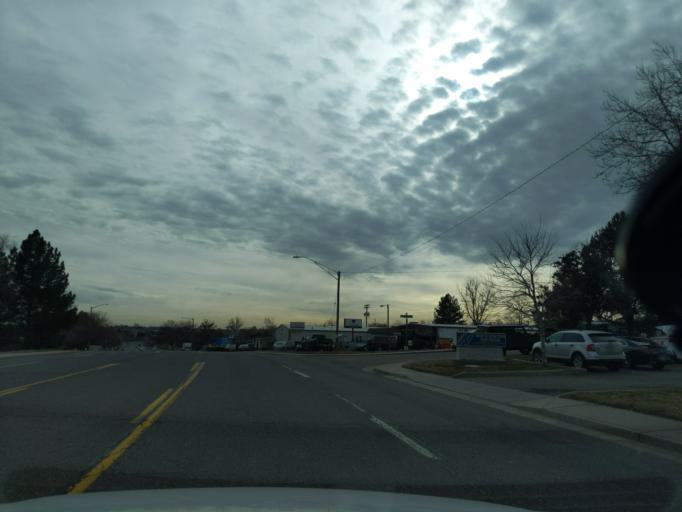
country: US
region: Colorado
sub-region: Adams County
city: Northglenn
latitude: 39.8934
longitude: -104.9663
